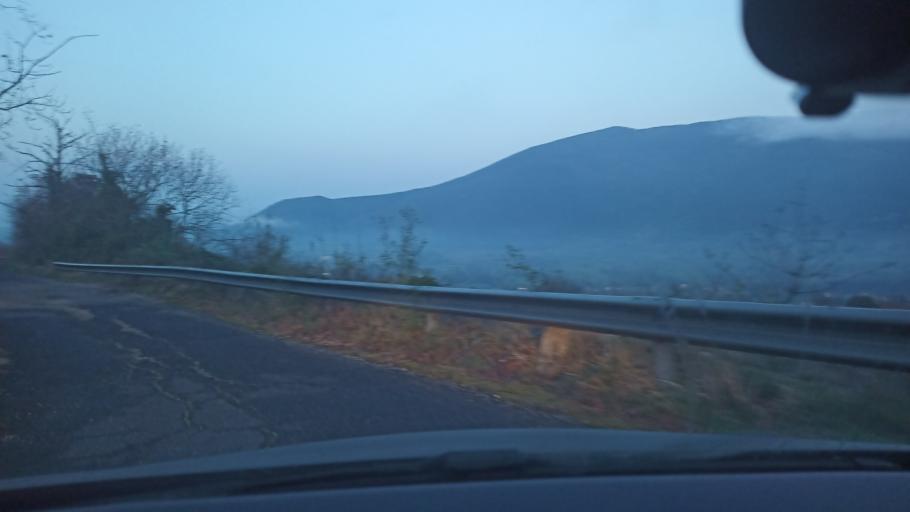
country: IT
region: Latium
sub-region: Provincia di Rieti
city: Cottanello
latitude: 42.4104
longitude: 12.6827
